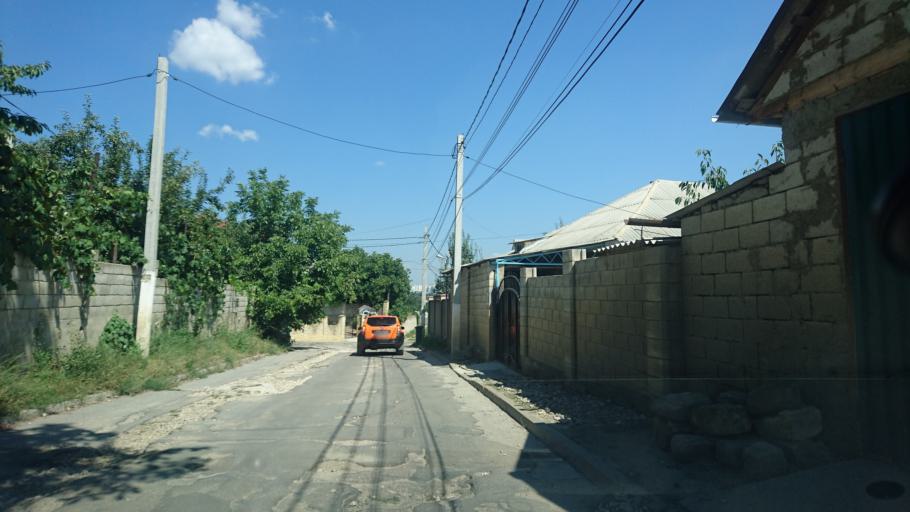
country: MD
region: Chisinau
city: Vatra
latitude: 47.0124
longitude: 28.7669
